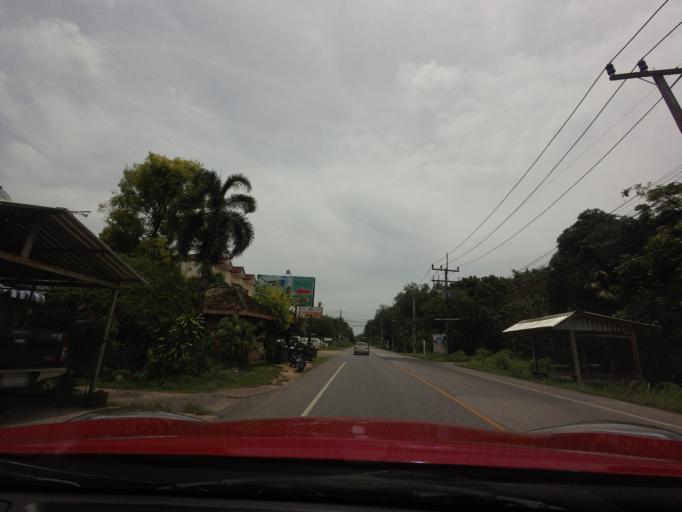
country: TH
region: Songkhla
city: Na Mom
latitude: 7.0023
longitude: 100.5290
